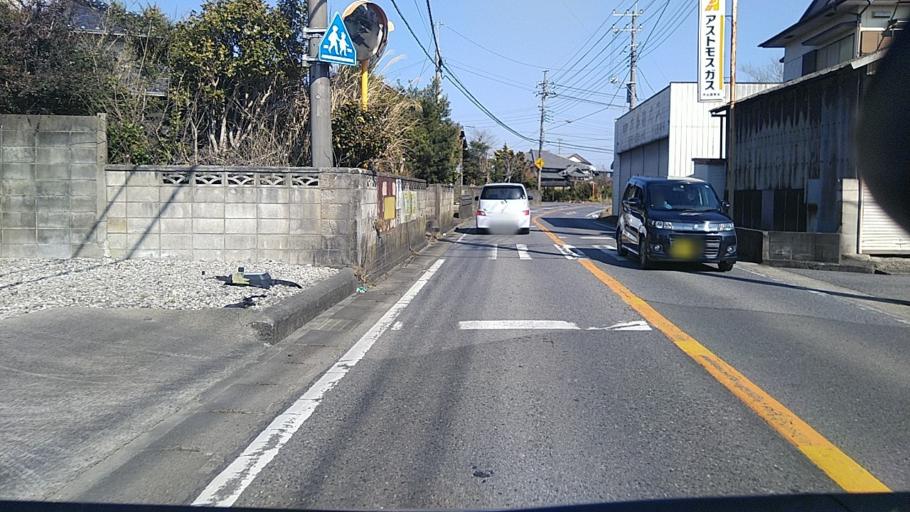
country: JP
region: Chiba
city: Mobara
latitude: 35.4238
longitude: 140.2666
